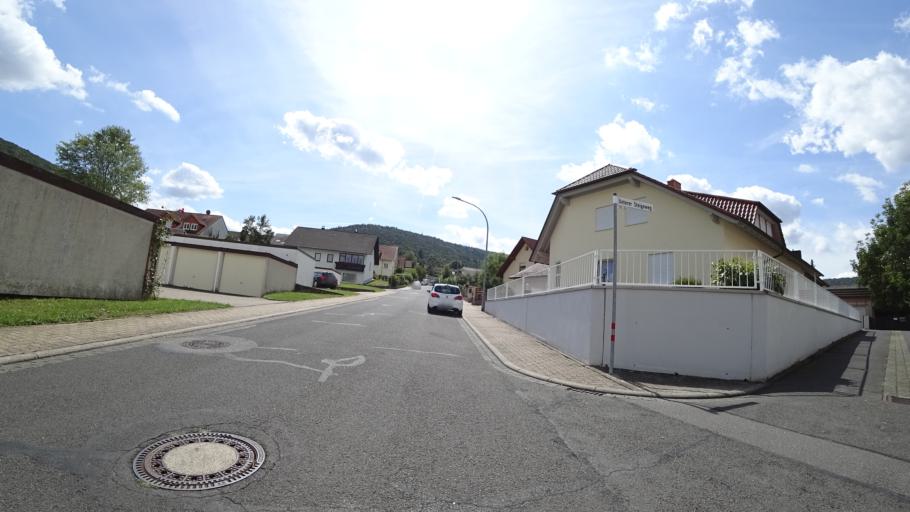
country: DE
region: Bavaria
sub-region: Regierungsbezirk Unterfranken
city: Miltenberg
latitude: 49.7021
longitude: 9.2729
